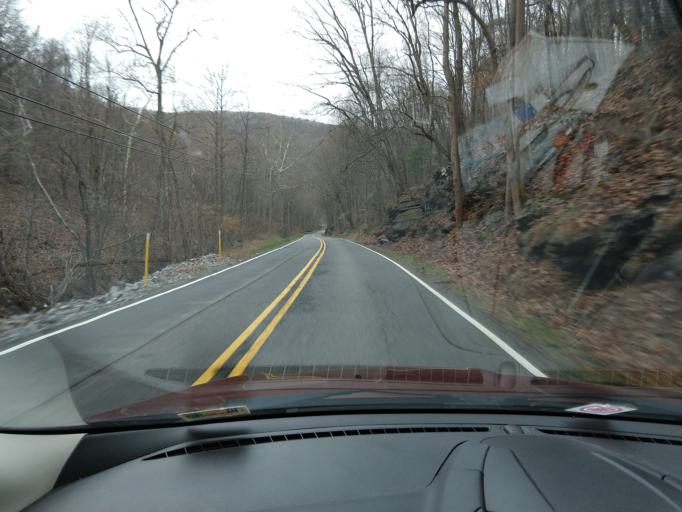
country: US
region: West Virginia
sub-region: Greenbrier County
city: White Sulphur Springs
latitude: 37.7418
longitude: -80.2292
